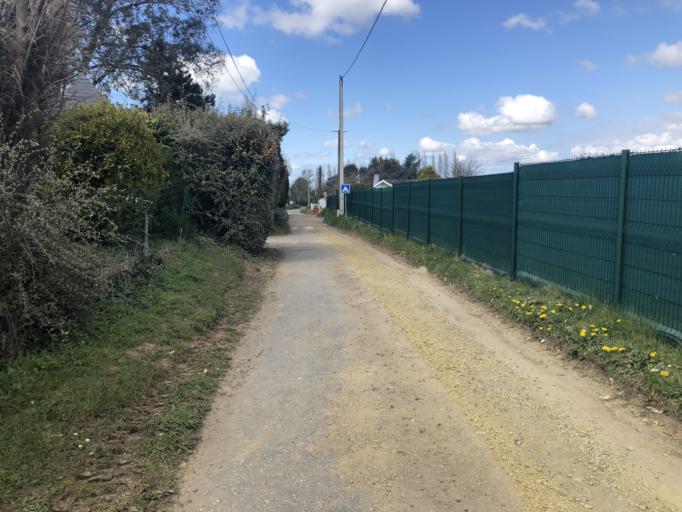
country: FR
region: Haute-Normandie
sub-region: Departement de la Seine-Maritime
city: Octeville-sur-Mer
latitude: 49.5450
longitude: 0.1193
